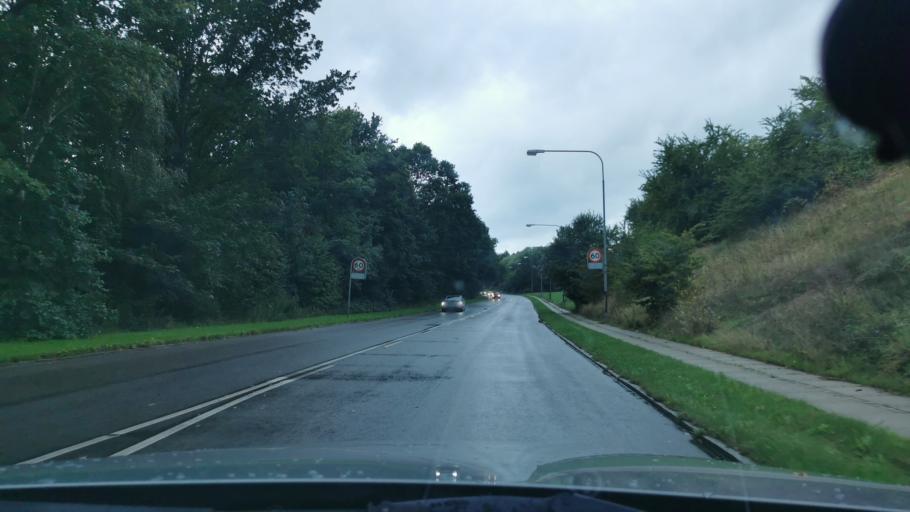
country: DK
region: Zealand
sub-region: Kalundborg Kommune
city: Kalundborg
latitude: 55.6869
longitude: 11.0733
